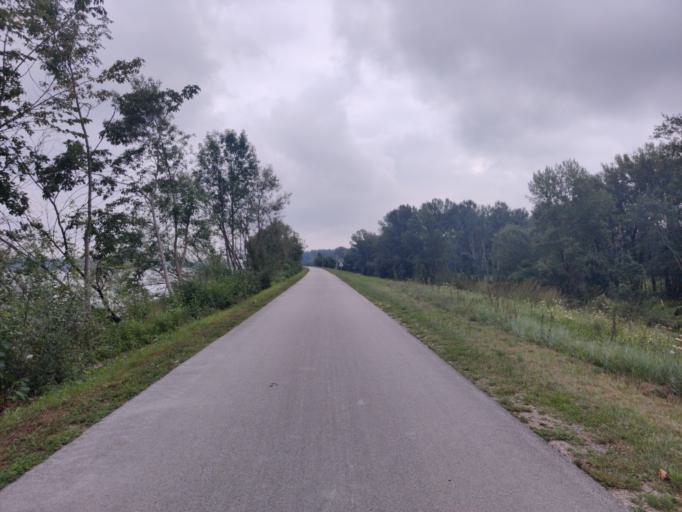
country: AT
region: Lower Austria
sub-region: Politischer Bezirk Tulln
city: Grafenworth
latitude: 48.3740
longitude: 15.7747
